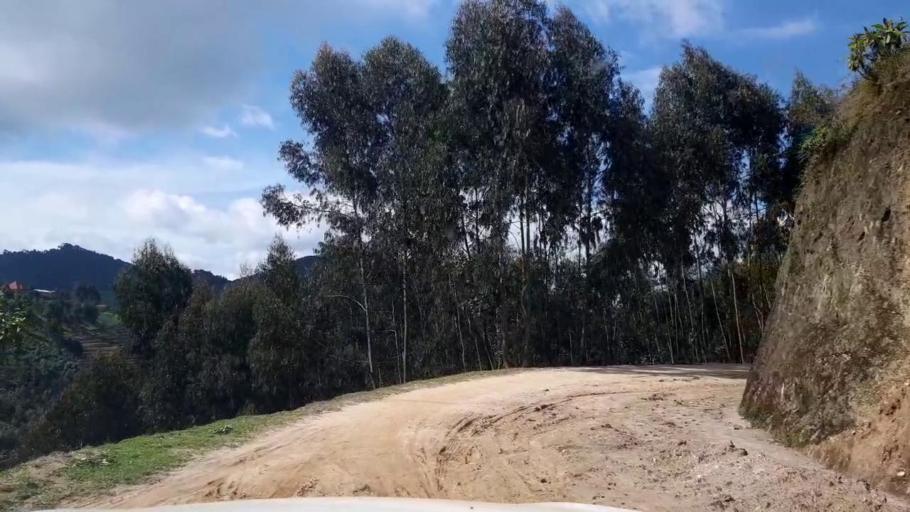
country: RW
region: Western Province
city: Kibuye
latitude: -1.8836
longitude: 29.4821
